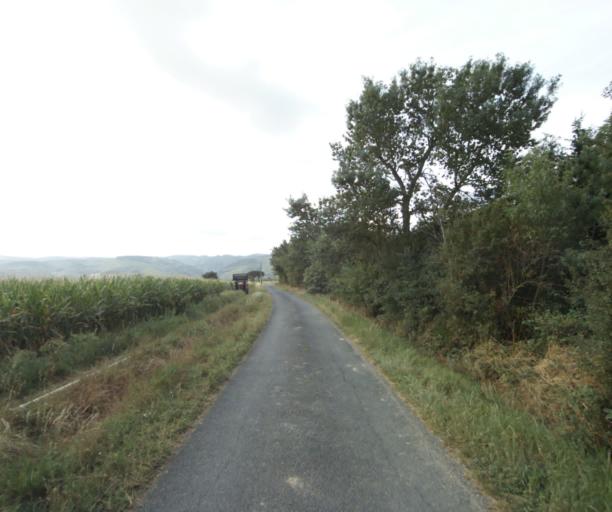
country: FR
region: Midi-Pyrenees
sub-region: Departement du Tarn
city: Soreze
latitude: 43.4825
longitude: 2.0889
